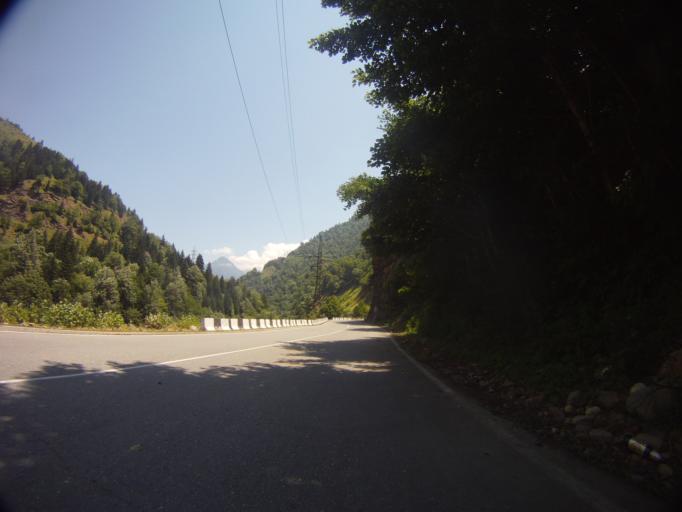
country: GE
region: Samegrelo and Zemo Svaneti
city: Jvari
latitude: 42.9306
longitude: 42.1135
